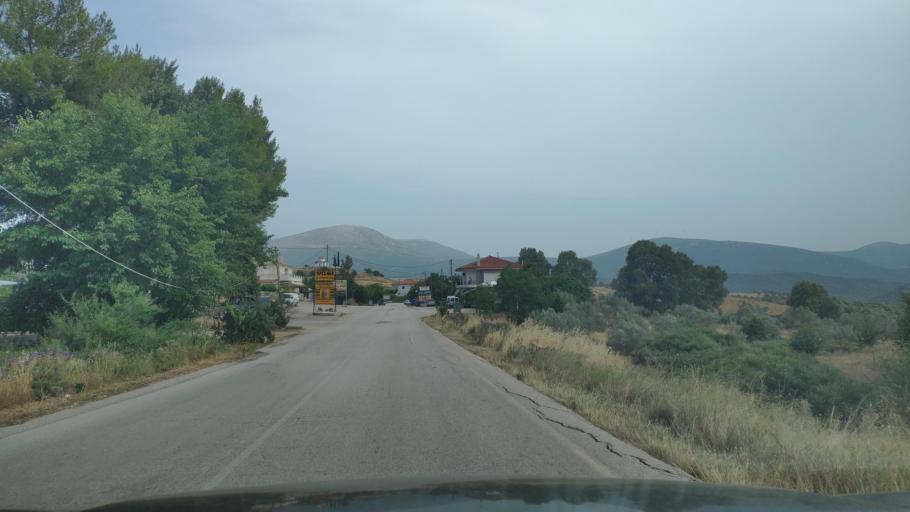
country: GR
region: Peloponnese
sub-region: Nomos Argolidos
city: Palaia Epidavros
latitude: 37.5629
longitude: 23.1518
